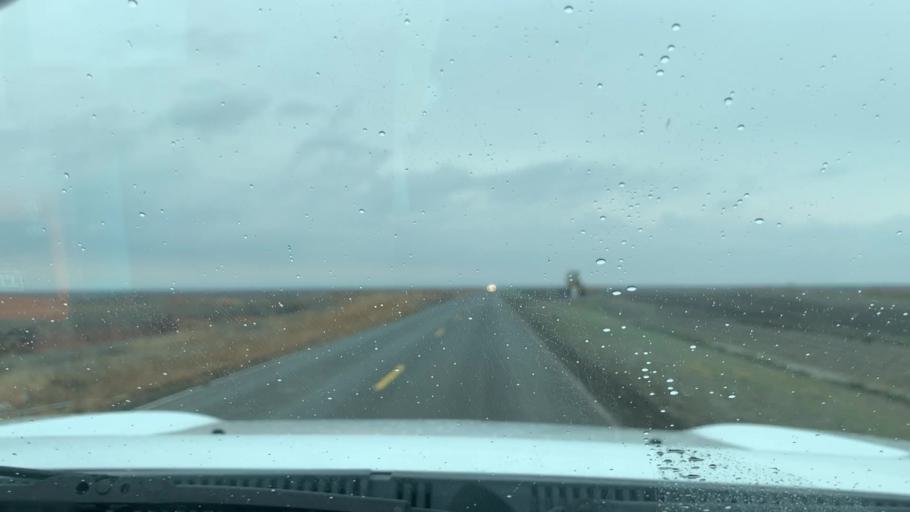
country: US
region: California
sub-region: Kings County
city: Kettleman City
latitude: 35.9339
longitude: -119.7347
